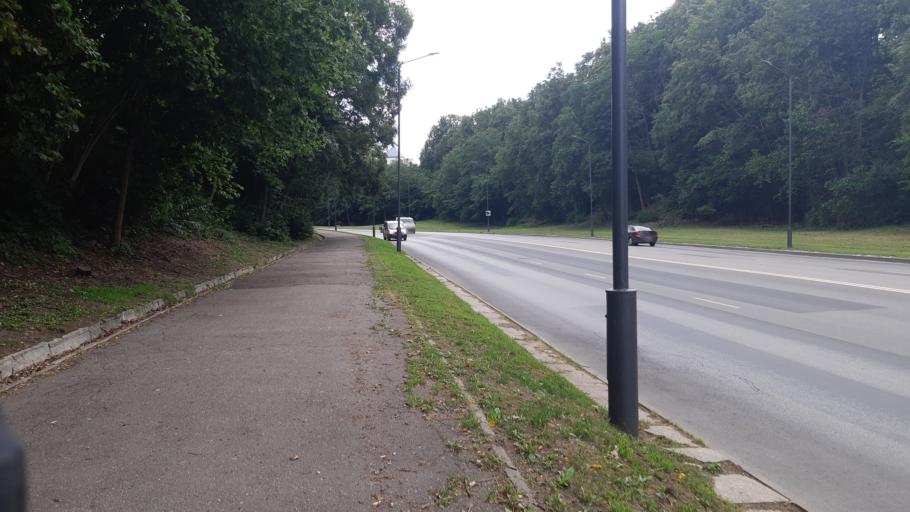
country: LT
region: Kauno apskritis
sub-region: Kaunas
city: Eiguliai
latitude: 54.9293
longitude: 23.9198
